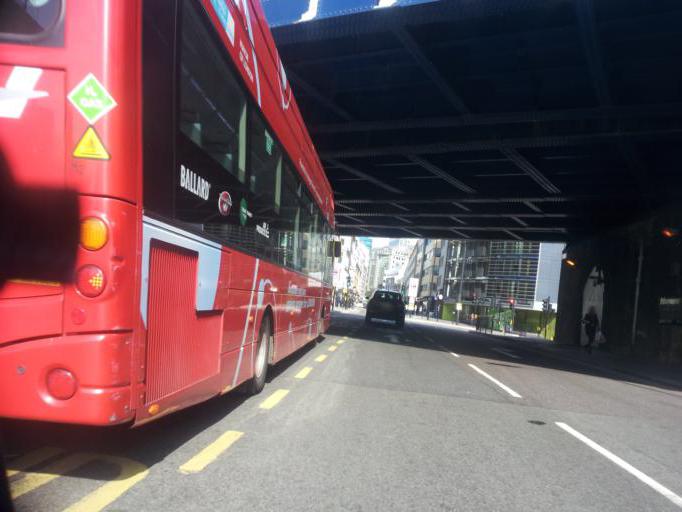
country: GB
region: England
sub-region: Greater London
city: City of London
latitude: 51.5107
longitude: -0.0749
